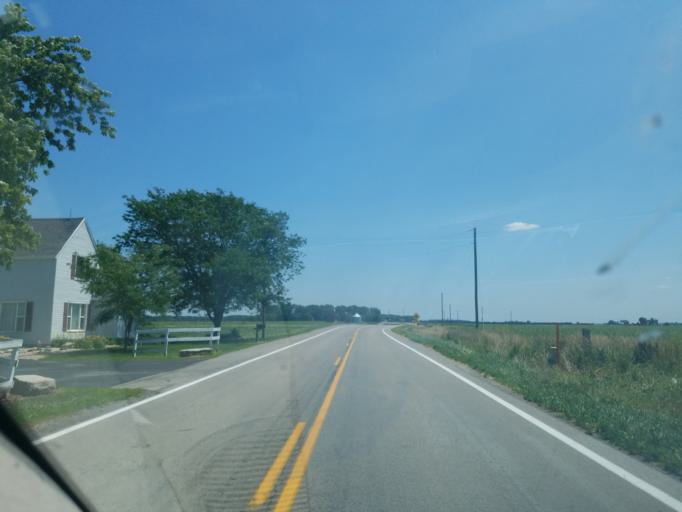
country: US
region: Ohio
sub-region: Allen County
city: Spencerville
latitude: 40.7426
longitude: -84.4589
